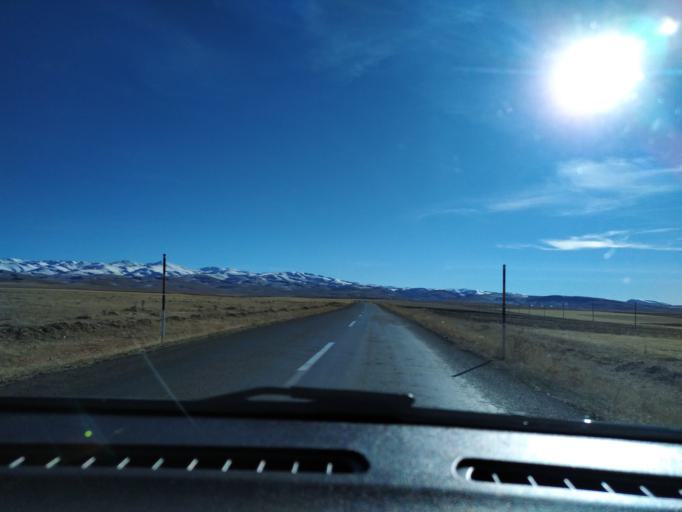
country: TR
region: Kayseri
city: Orensehir
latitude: 38.8956
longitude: 36.7293
